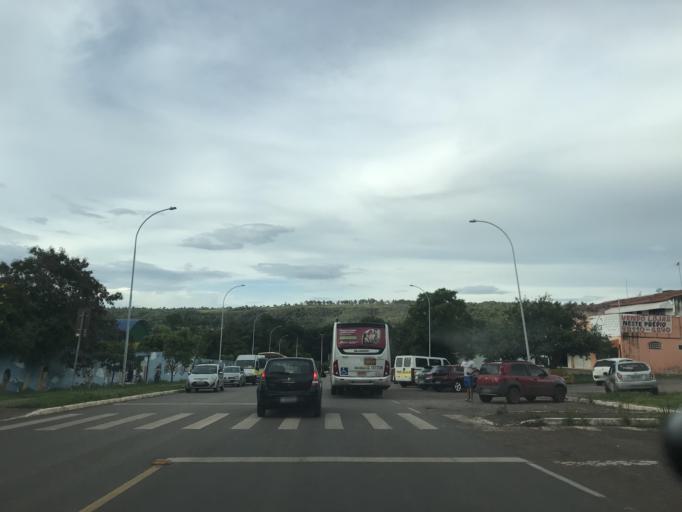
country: BR
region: Federal District
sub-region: Brasilia
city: Brasilia
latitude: -15.6407
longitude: -47.8018
